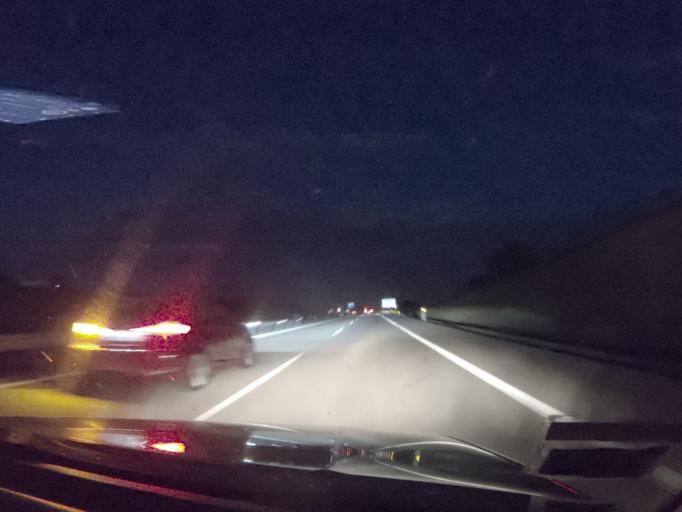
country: ES
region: Castille and Leon
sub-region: Provincia de Leon
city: Brazuelo
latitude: 42.4826
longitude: -6.1094
